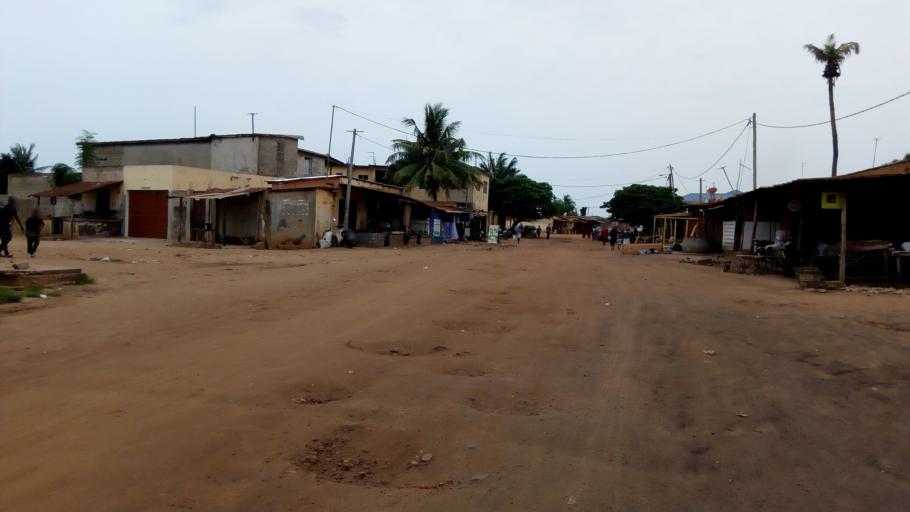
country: TG
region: Maritime
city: Lome
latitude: 6.1606
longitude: 1.2147
